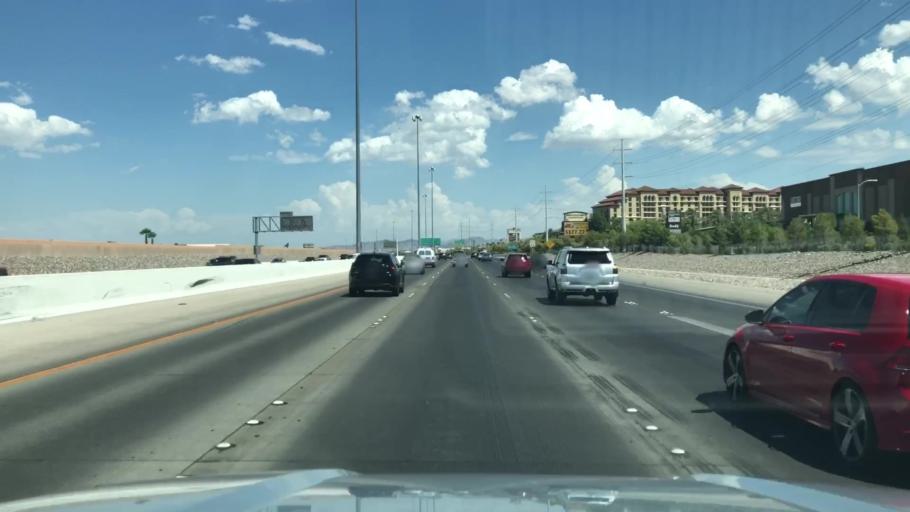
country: US
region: Nevada
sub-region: Clark County
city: Whitney
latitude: 36.0234
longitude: -115.0955
